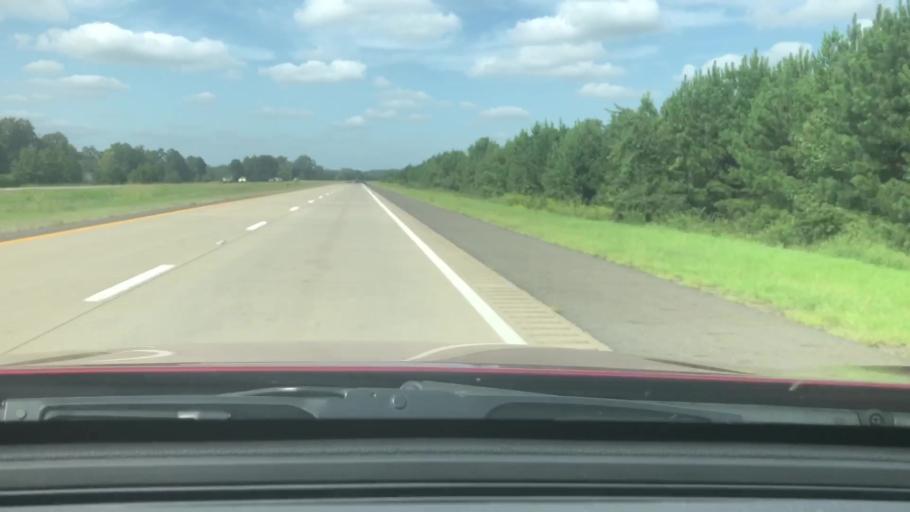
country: US
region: Texas
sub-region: Cass County
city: Queen City
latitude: 33.1929
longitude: -93.8773
